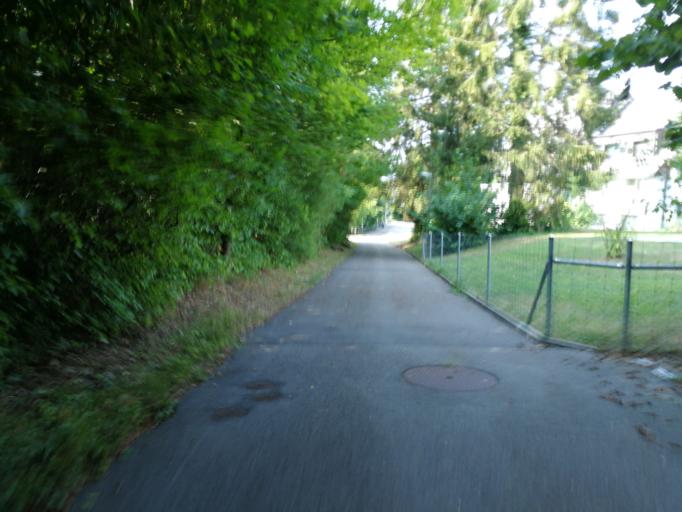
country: CH
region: Zurich
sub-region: Bezirk Meilen
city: Uetikon
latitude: 47.2676
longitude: 8.6859
